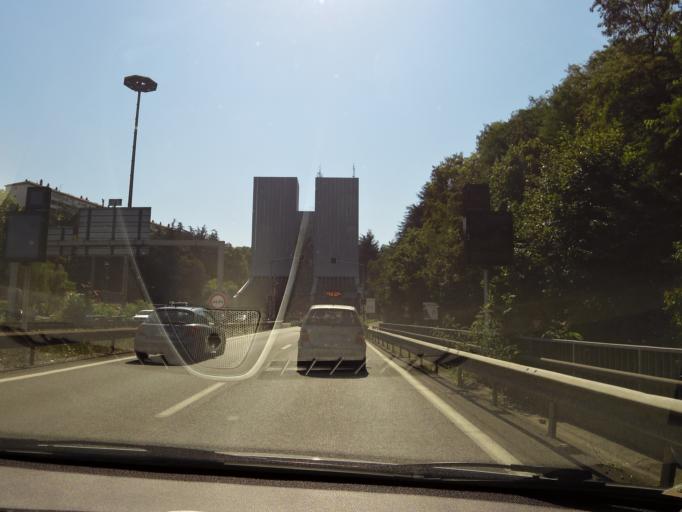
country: FR
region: Rhone-Alpes
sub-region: Departement du Rhone
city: Tassin-la-Demi-Lune
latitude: 45.7643
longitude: 4.8015
